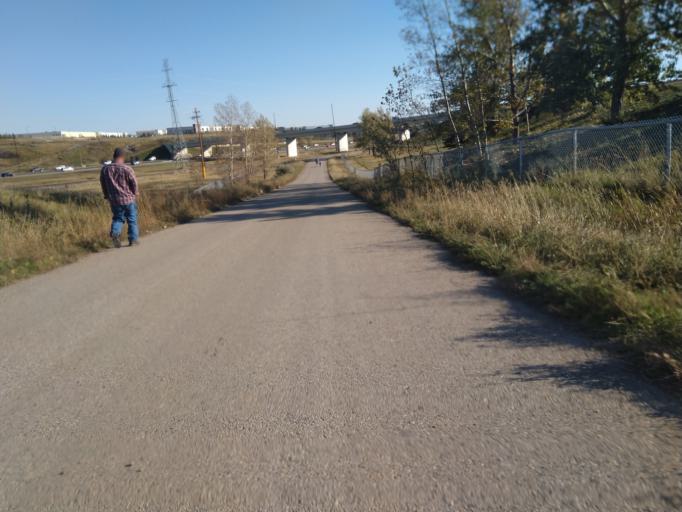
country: CA
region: Alberta
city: Calgary
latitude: 51.1276
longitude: -114.0497
